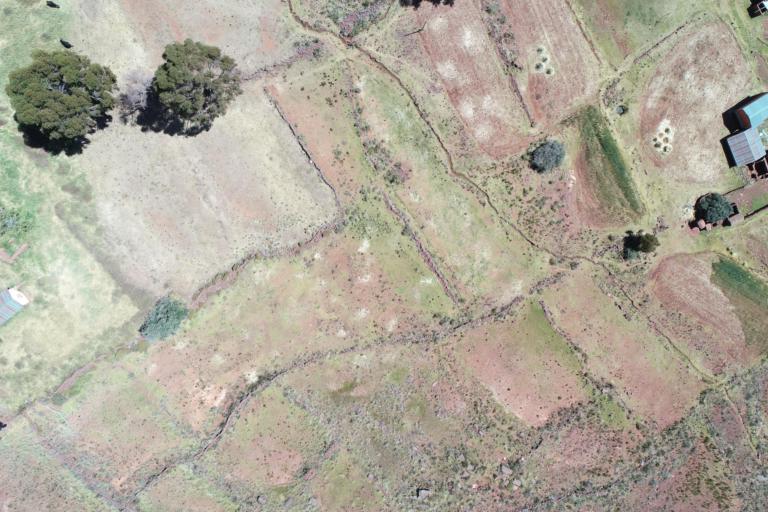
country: BO
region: La Paz
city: Tiahuanaco
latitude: -16.6036
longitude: -68.7719
